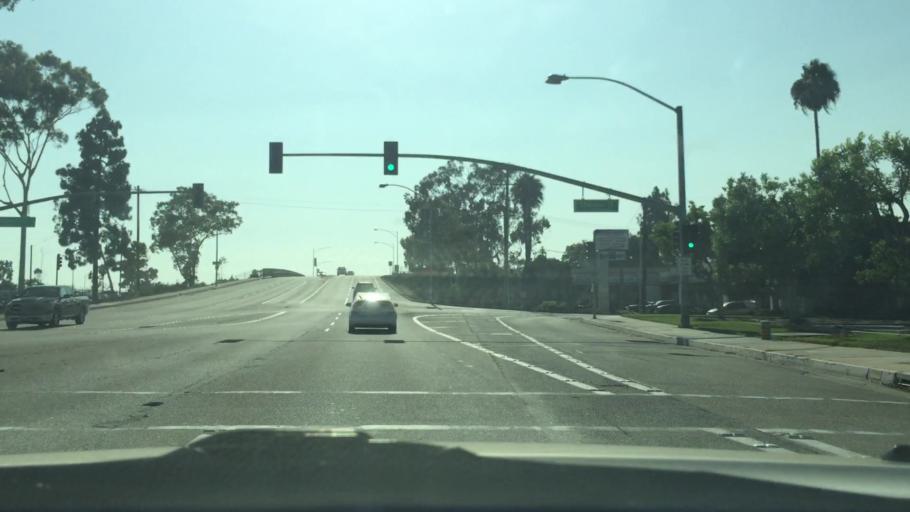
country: US
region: California
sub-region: Orange County
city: Midway City
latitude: 33.7447
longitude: -118.0020
